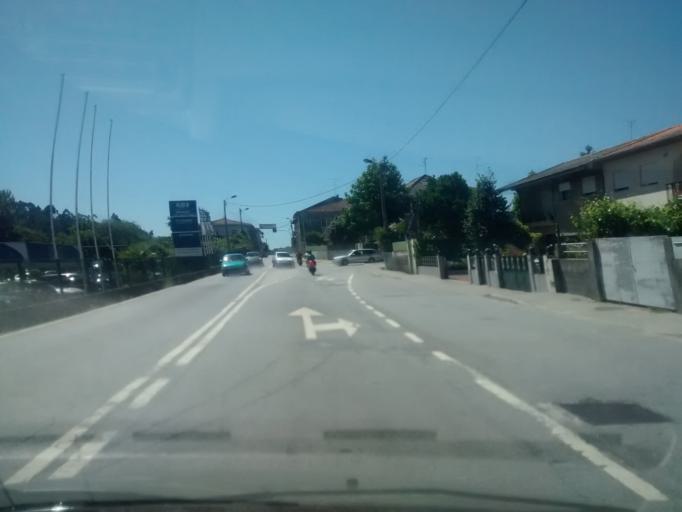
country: PT
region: Braga
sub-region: Braga
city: Oliveira
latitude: 41.5333
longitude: -8.4944
